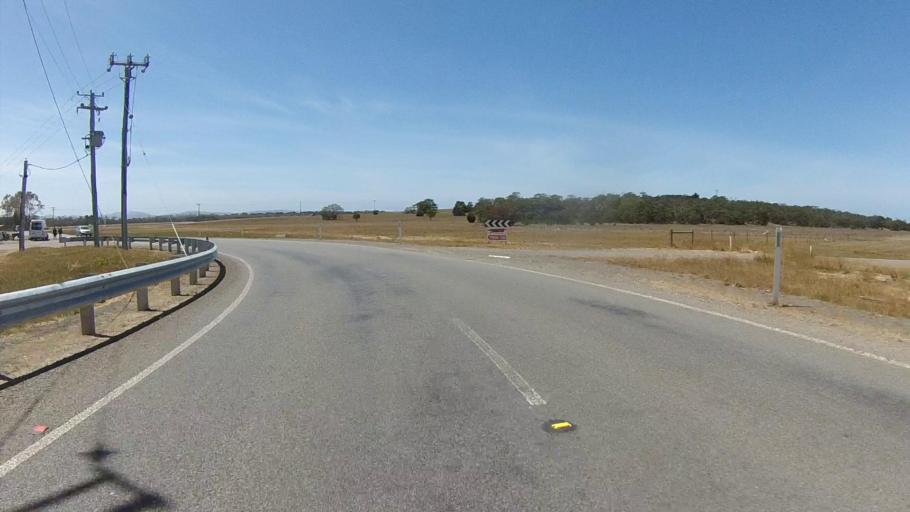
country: AU
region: Tasmania
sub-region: Clarence
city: Seven Mile Beach
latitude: -42.8316
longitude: 147.4960
